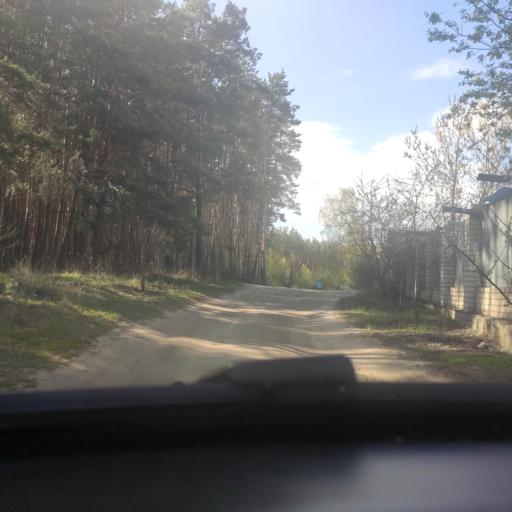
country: RU
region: Voronezj
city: Somovo
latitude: 51.7522
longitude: 39.3220
